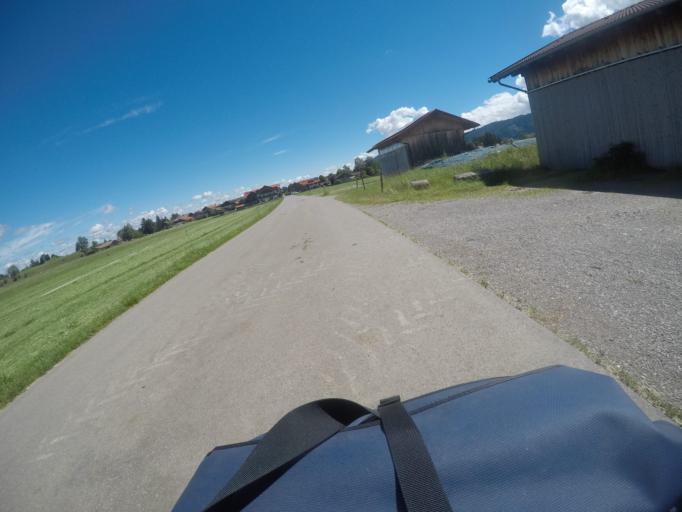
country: DE
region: Bavaria
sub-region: Swabia
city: Schwangau
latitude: 47.5916
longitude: 10.7374
